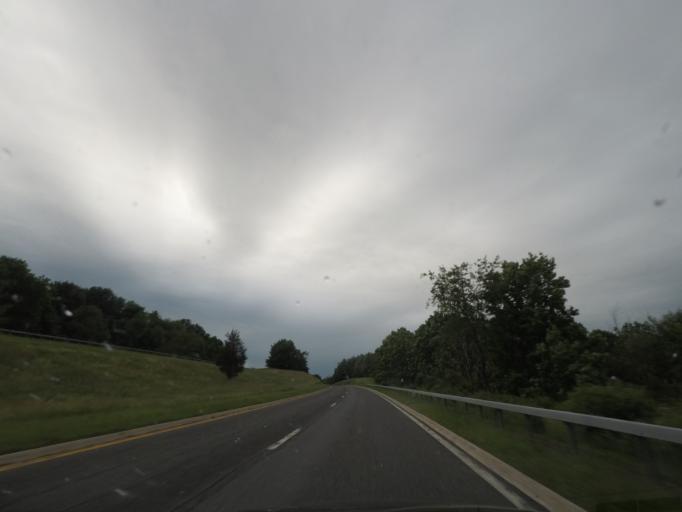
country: US
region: New York
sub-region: Columbia County
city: Chatham
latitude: 42.3341
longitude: -73.5677
